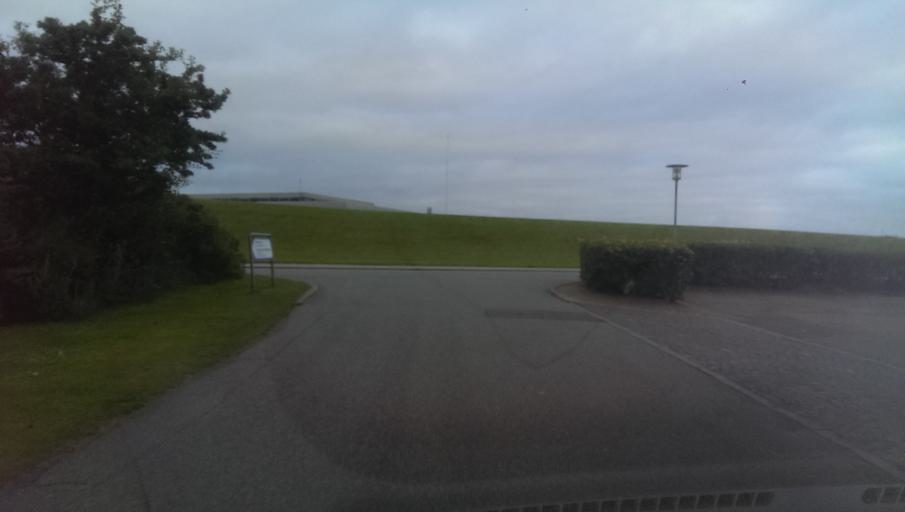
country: DK
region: South Denmark
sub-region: Esbjerg Kommune
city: Esbjerg
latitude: 55.4931
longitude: 8.4541
